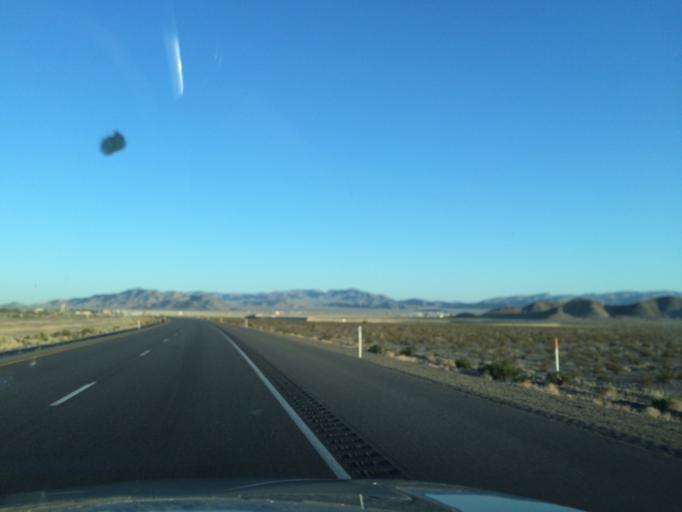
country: US
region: Nevada
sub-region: Nye County
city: Pahrump
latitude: 36.5753
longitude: -115.6393
